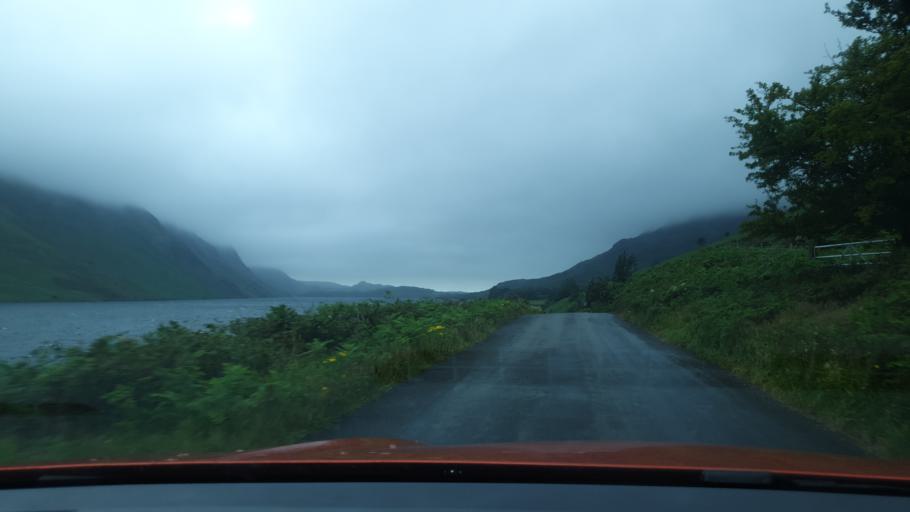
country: GB
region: England
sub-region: Cumbria
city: Keswick
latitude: 54.4547
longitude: -3.2713
